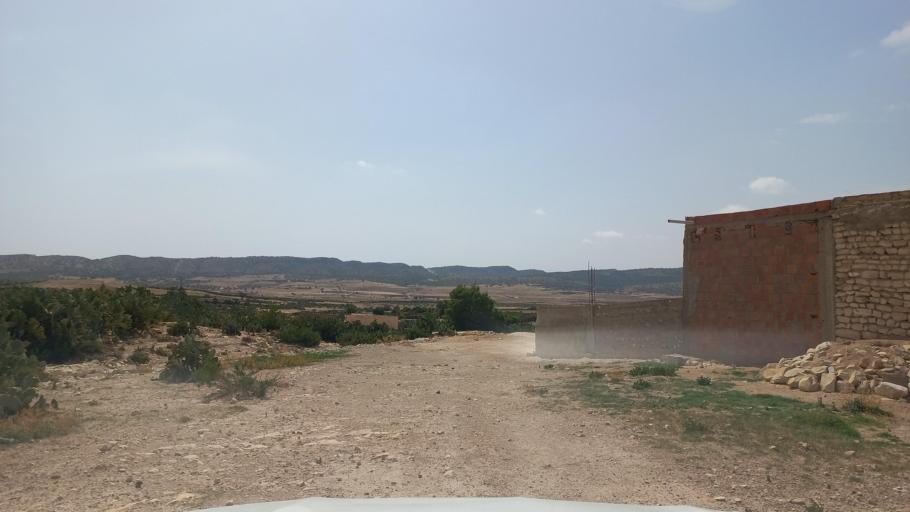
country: TN
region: Al Qasrayn
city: Sbiba
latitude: 35.4040
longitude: 8.9696
